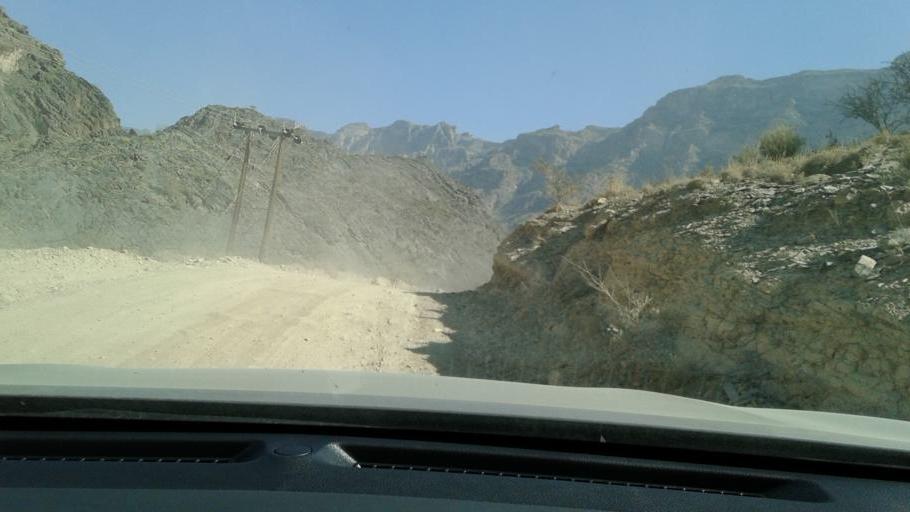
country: OM
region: Al Batinah
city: Bayt al `Awabi
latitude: 23.1916
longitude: 57.3980
